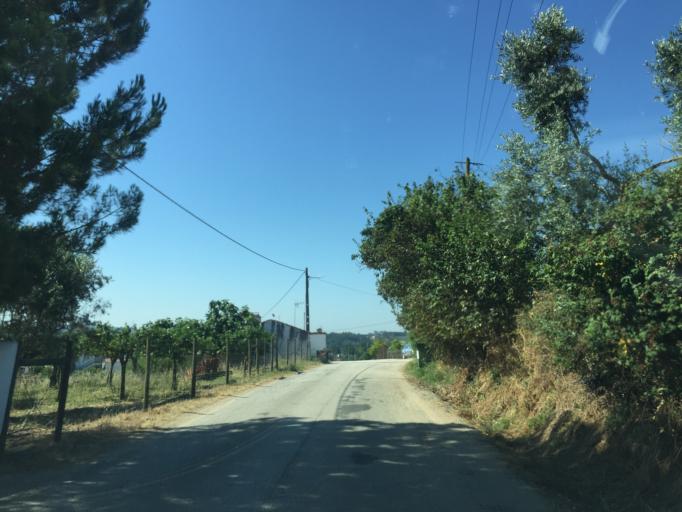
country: PT
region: Santarem
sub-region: Constancia
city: Constancia
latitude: 39.5549
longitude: -8.3154
